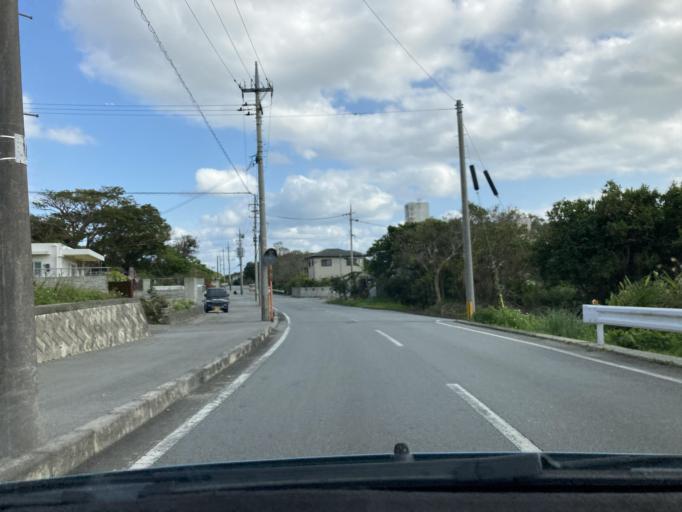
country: JP
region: Okinawa
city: Tomigusuku
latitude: 26.1709
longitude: 127.7605
